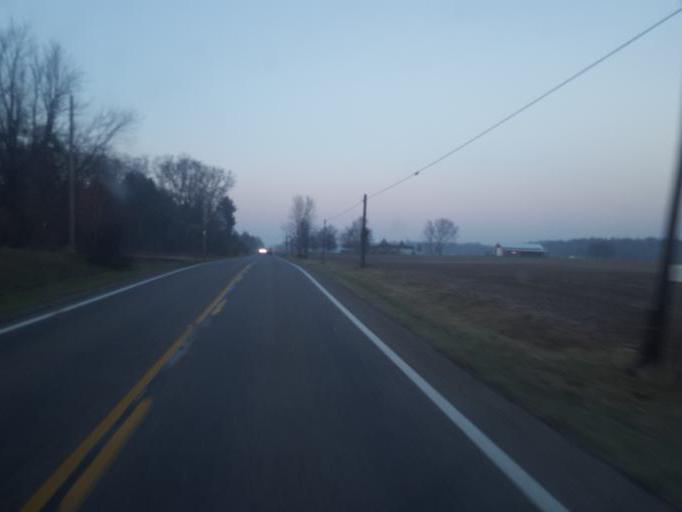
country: US
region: Ohio
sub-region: Morrow County
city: Cardington
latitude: 40.4252
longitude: -82.8250
